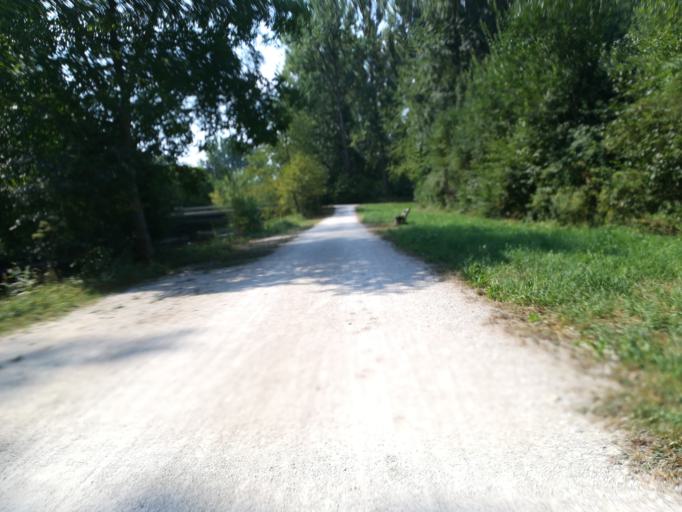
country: DE
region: Baden-Wuerttemberg
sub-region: Freiburg Region
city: Singen
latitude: 47.7820
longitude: 8.8336
